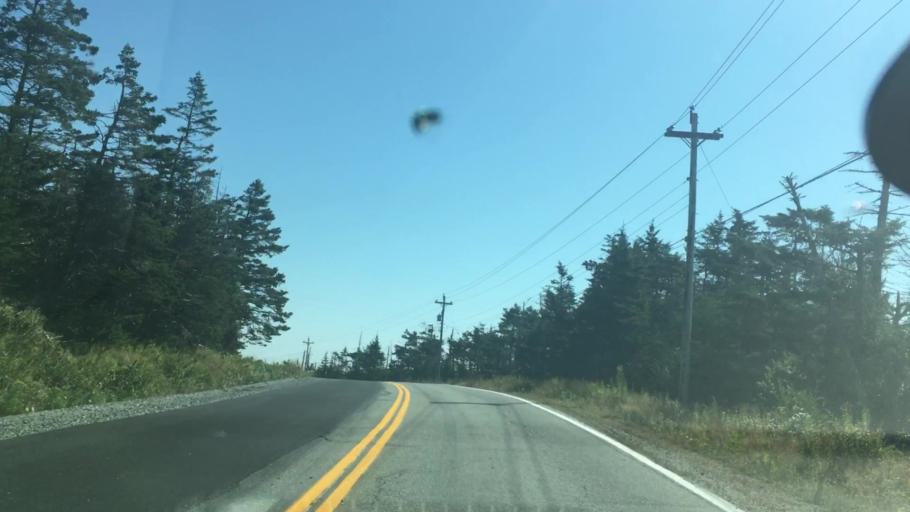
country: CA
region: Nova Scotia
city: New Glasgow
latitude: 44.9157
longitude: -62.3179
